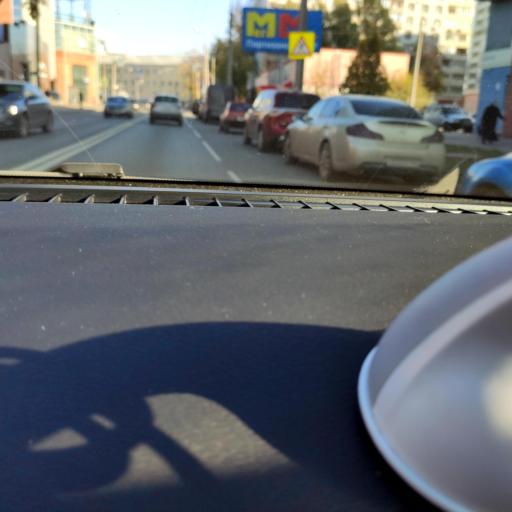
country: RU
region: Samara
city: Samara
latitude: 53.2015
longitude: 50.1430
